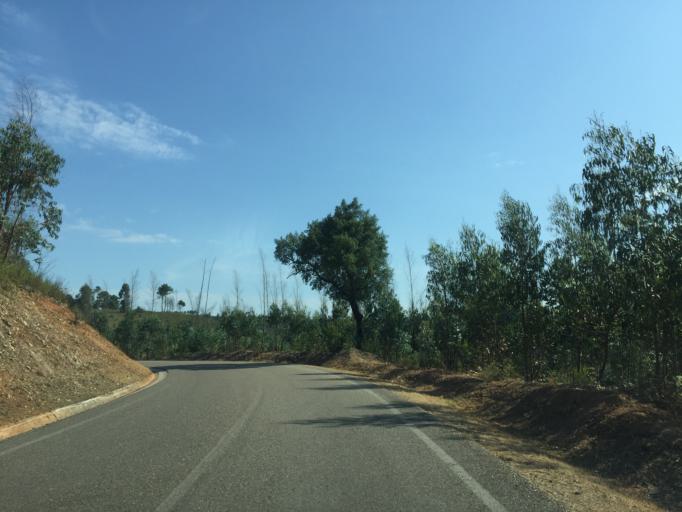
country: PT
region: Santarem
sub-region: Ferreira do Zezere
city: Ferreira do Zezere
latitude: 39.5823
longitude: -8.2963
